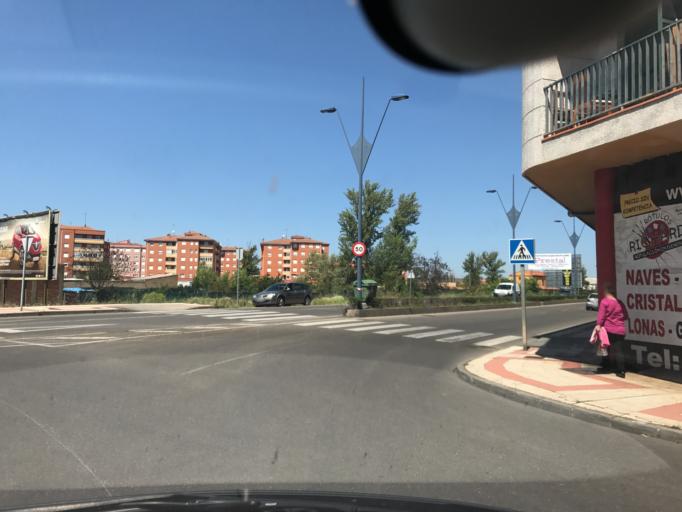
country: ES
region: Castille and Leon
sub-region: Provincia de Leon
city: San Andres del Rabanedo
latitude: 42.6020
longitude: -5.5964
